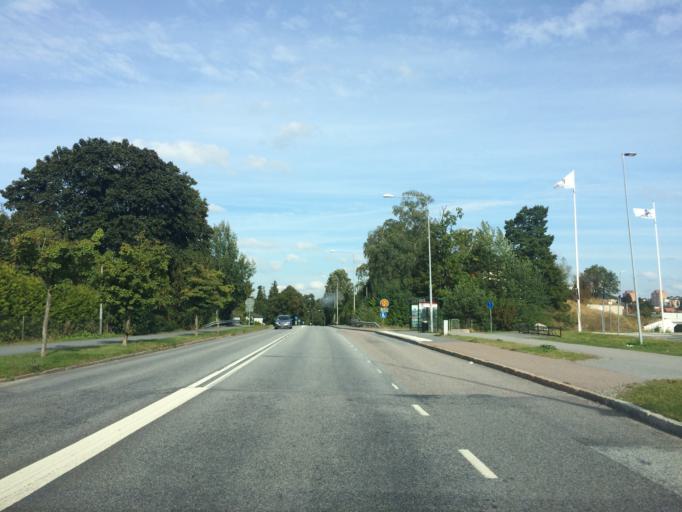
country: SE
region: Stockholm
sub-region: Sollentuna Kommun
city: Sollentuna
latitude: 59.4349
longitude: 17.9500
